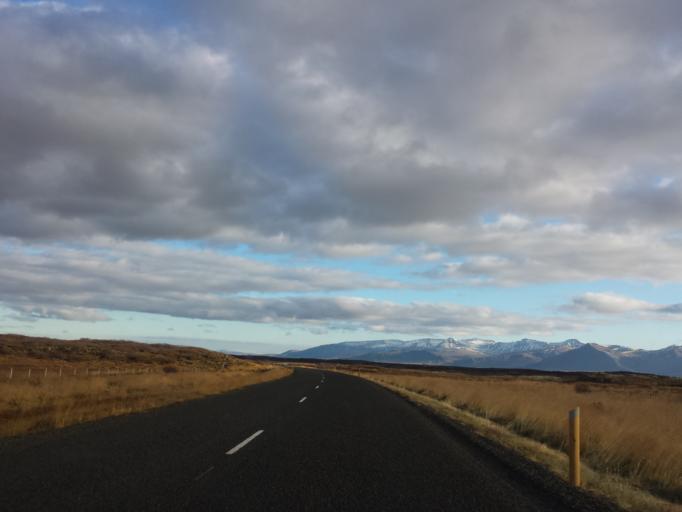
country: IS
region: West
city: Borgarnes
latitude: 64.6034
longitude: -22.0336
